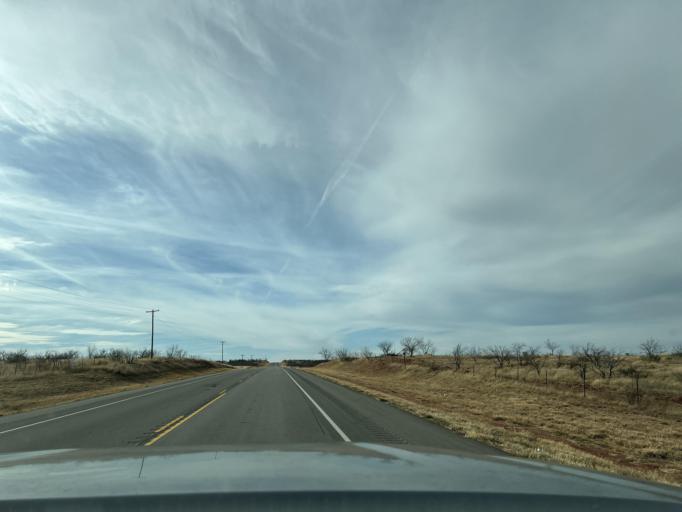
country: US
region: Texas
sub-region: Jones County
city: Anson
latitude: 32.7508
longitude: -99.7356
